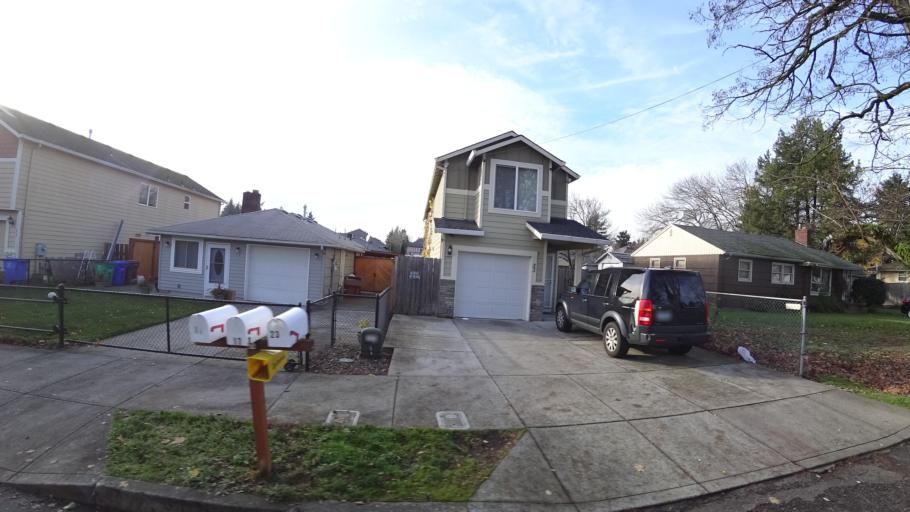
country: US
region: Oregon
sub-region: Multnomah County
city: Lents
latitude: 45.5227
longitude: -122.5158
